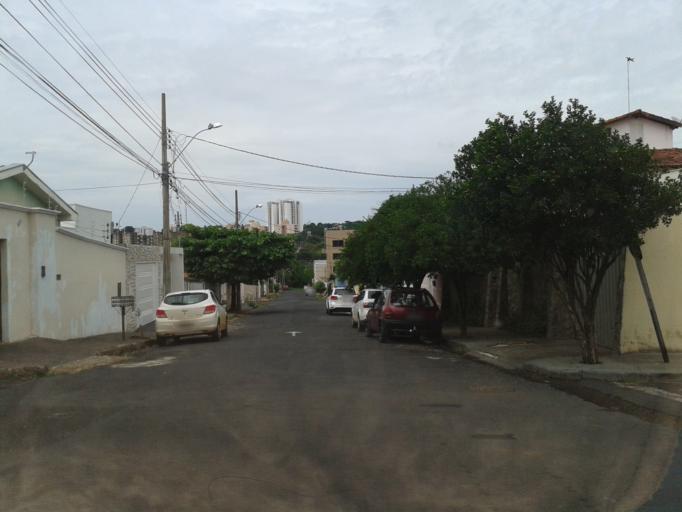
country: BR
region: Minas Gerais
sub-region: Uberlandia
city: Uberlandia
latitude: -18.9254
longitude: -48.2936
